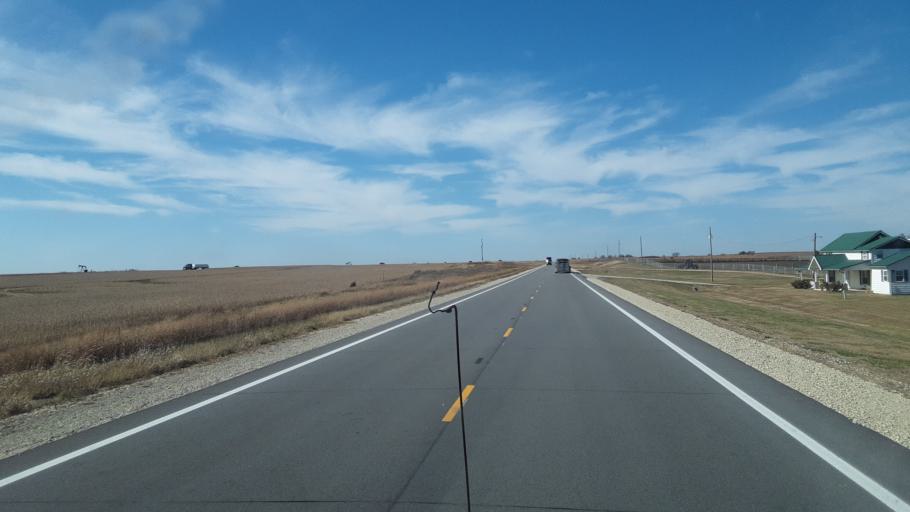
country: US
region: Kansas
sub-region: Marion County
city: Marion
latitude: 38.3627
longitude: -96.8103
